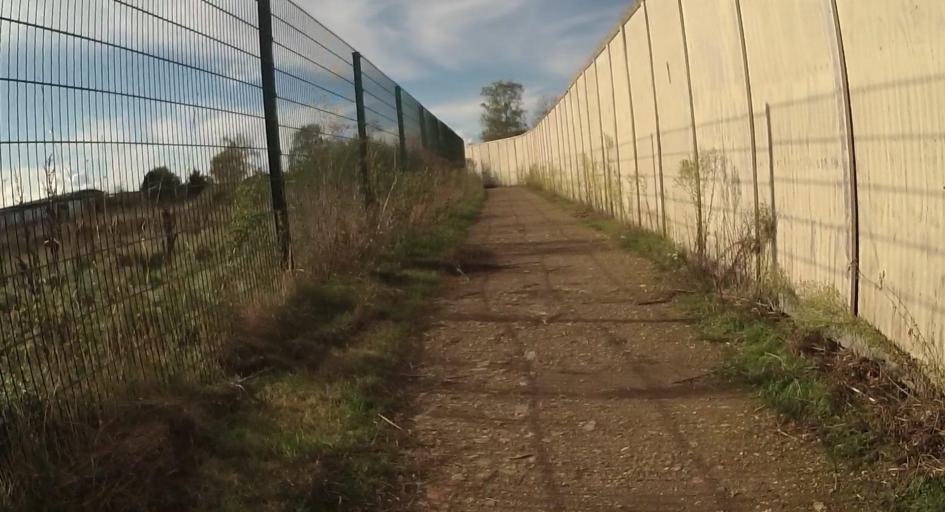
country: GB
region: England
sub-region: Wokingham
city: Barkham
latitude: 51.3812
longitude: -0.8901
